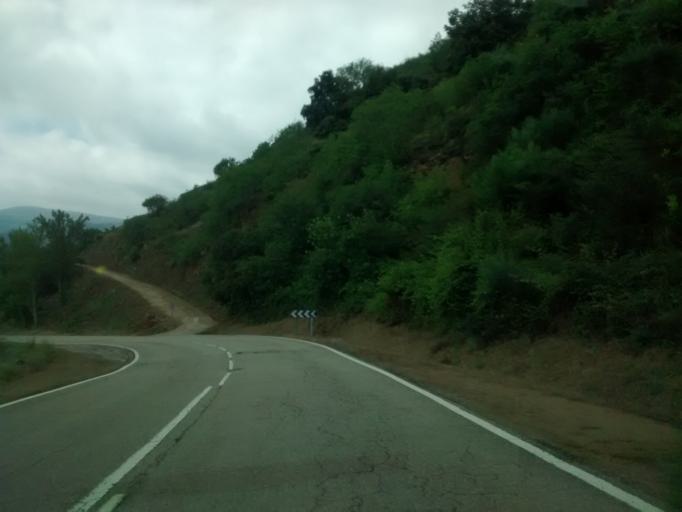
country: ES
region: Galicia
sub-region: Provincia de Ourense
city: Manzaneda
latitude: 42.3248
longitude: -7.2137
